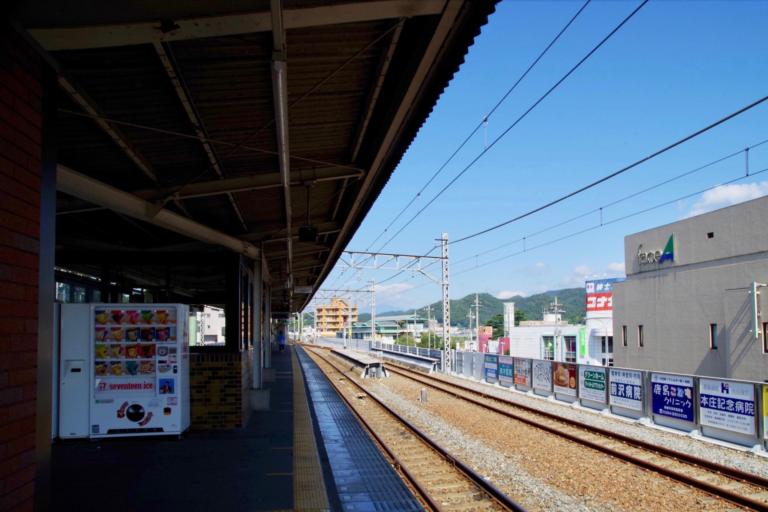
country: JP
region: Tochigi
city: Ashikaga
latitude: 36.3296
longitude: 139.4480
